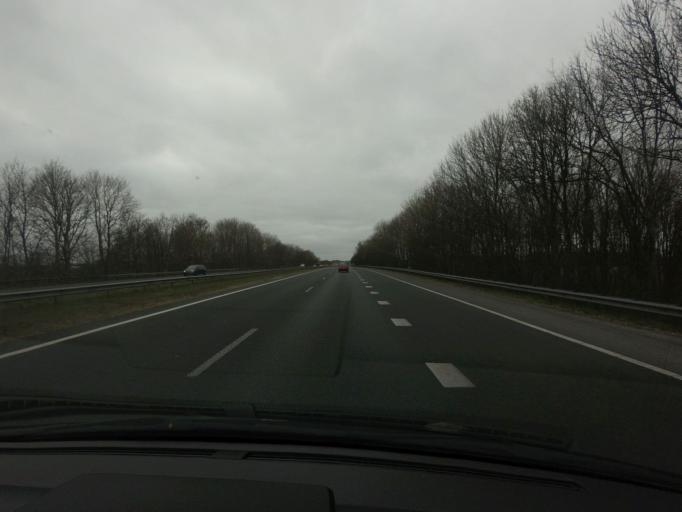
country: NL
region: Groningen
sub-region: Gemeente Hoogezand-Sappemeer
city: Hoogezand
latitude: 53.1789
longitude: 6.7314
